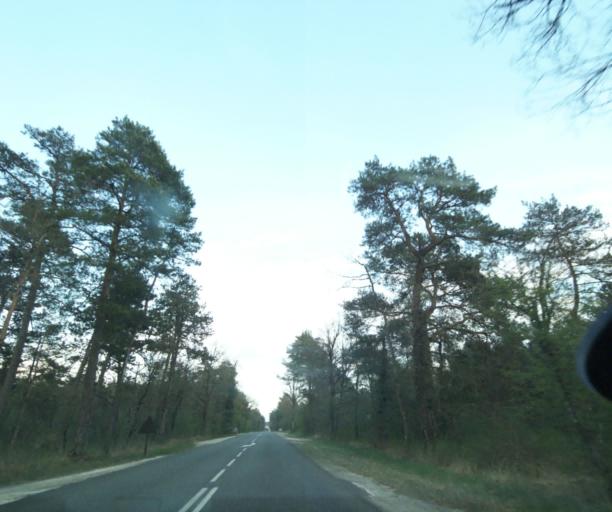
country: FR
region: Ile-de-France
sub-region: Departement de Seine-et-Marne
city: Avon
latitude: 48.3846
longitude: 2.7224
